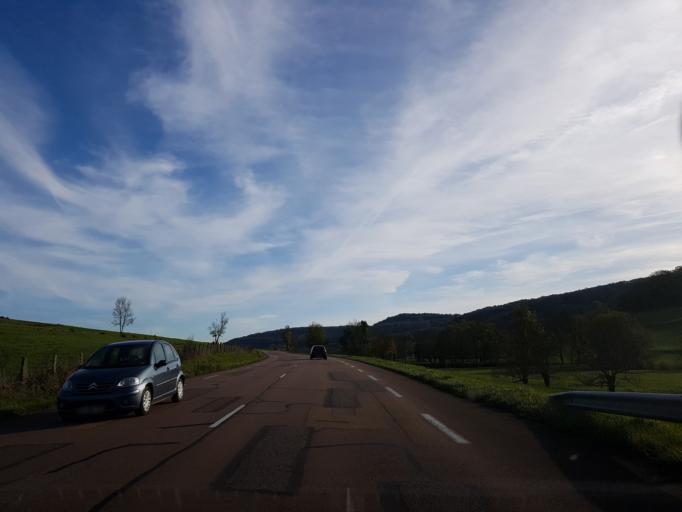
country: FR
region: Bourgogne
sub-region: Departement de la Cote-d'Or
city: Vitteaux
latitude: 47.3384
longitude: 4.5815
